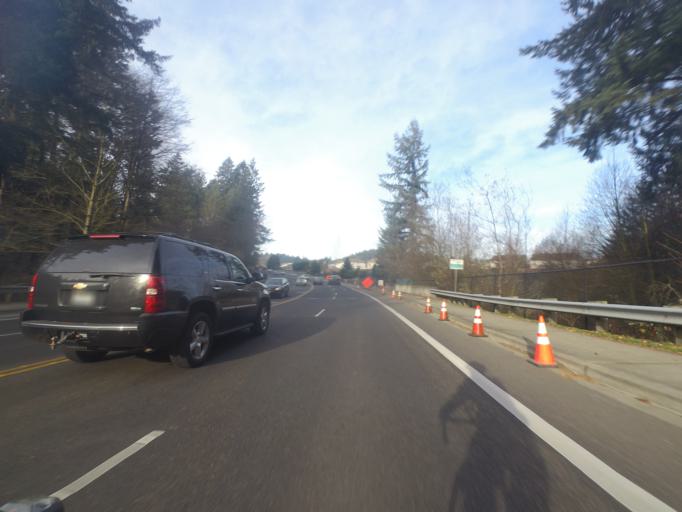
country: US
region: Washington
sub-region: Pierce County
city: Lakewood
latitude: 47.1980
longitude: -122.5223
